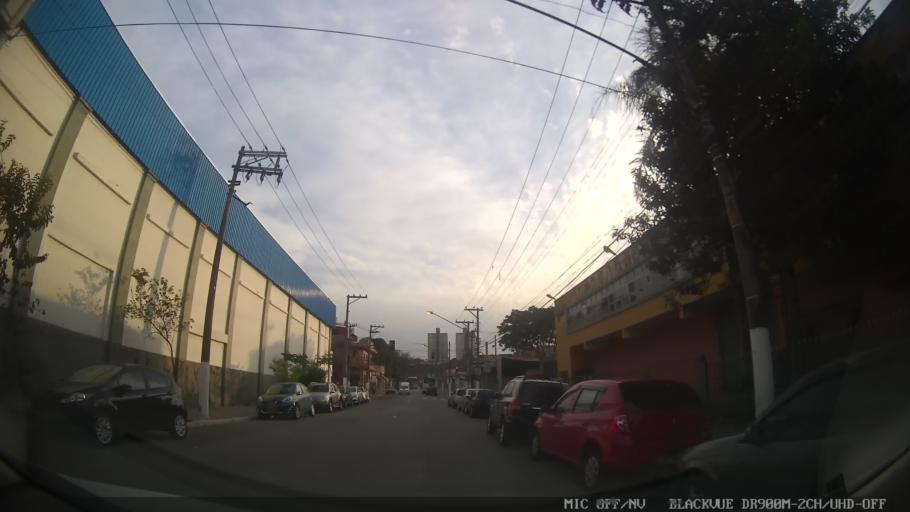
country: BR
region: Sao Paulo
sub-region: Sao Caetano Do Sul
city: Sao Caetano do Sul
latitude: -23.6031
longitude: -46.5905
